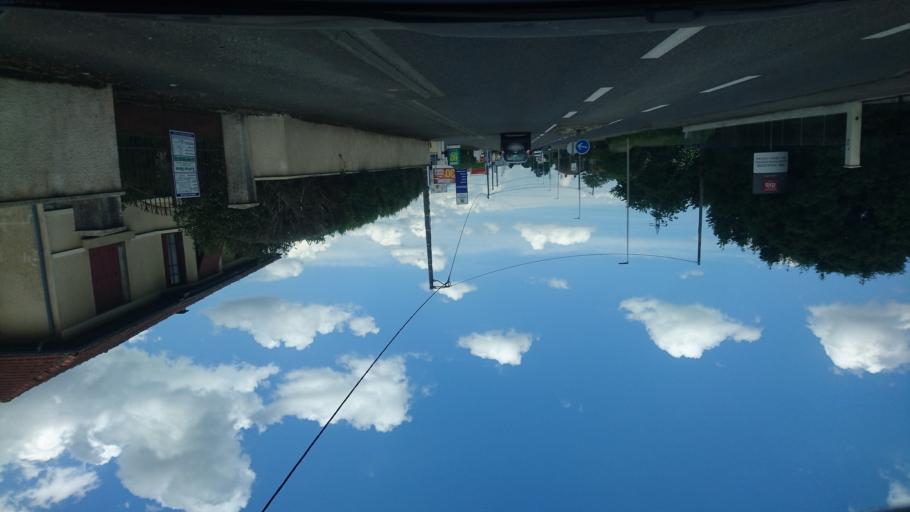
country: FR
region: Midi-Pyrenees
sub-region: Departement des Hautes-Pyrenees
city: Ibos
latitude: 43.2387
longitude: 0.0349
